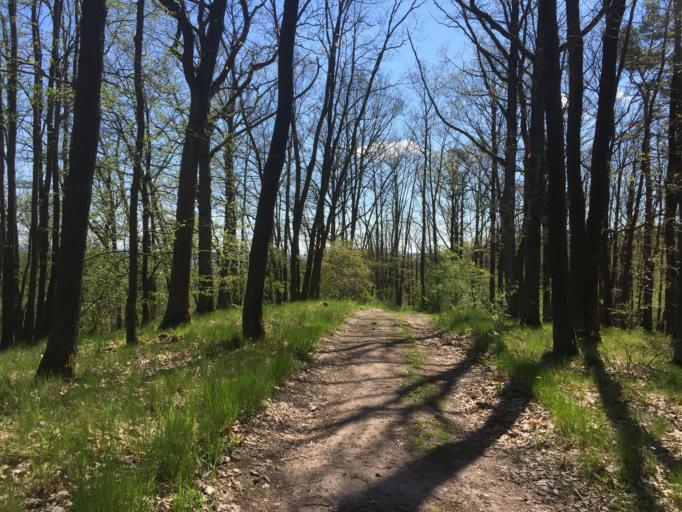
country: DE
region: Bavaria
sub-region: Regierungsbezirk Unterfranken
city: Sulzfeld
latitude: 50.2740
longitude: 10.4183
